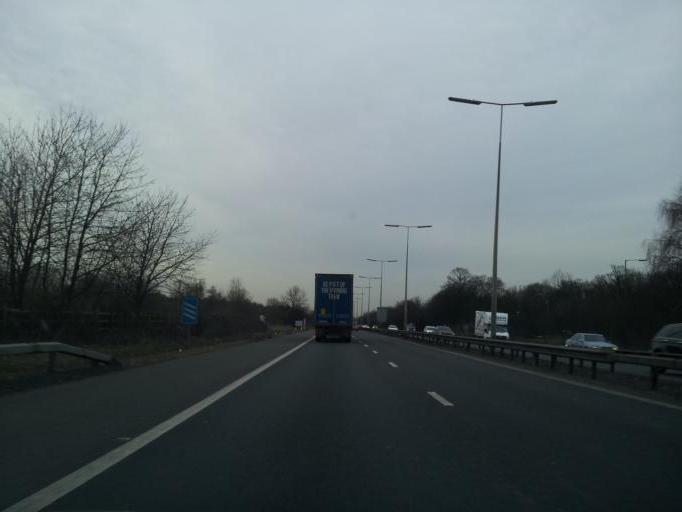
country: GB
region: England
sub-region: Hertfordshire
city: Hatfield
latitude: 51.7451
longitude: -0.2418
